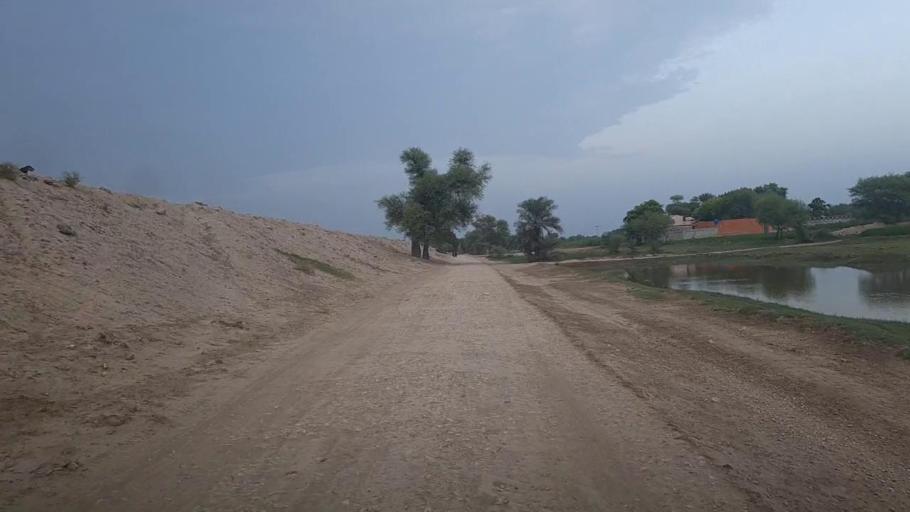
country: PK
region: Sindh
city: Kashmor
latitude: 28.3829
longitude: 69.7926
